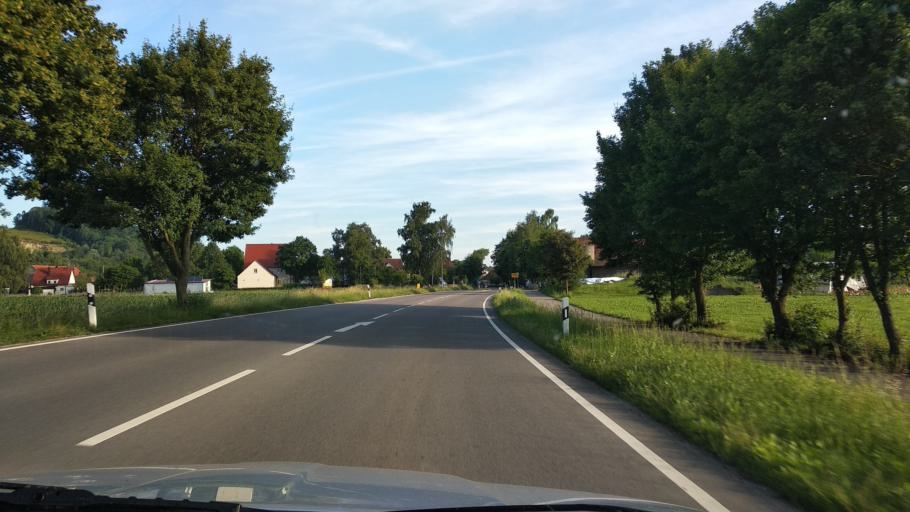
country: DE
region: Bavaria
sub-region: Swabia
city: Altenstadt
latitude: 48.1779
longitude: 10.1084
